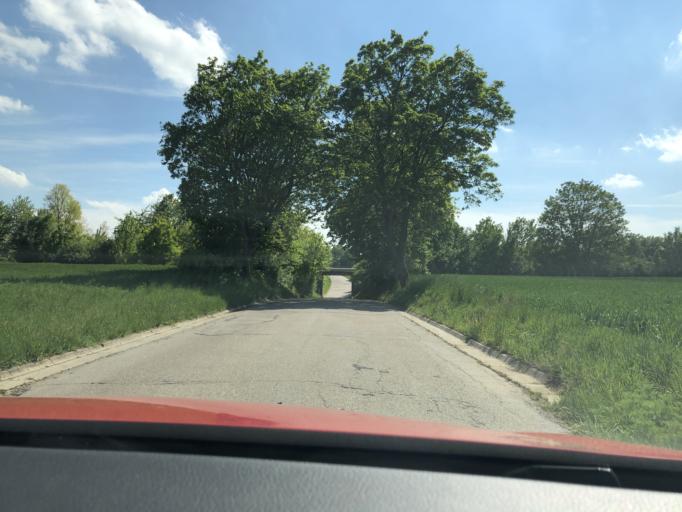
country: DE
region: Bavaria
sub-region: Upper Bavaria
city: Lenting
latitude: 48.7785
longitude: 11.4881
